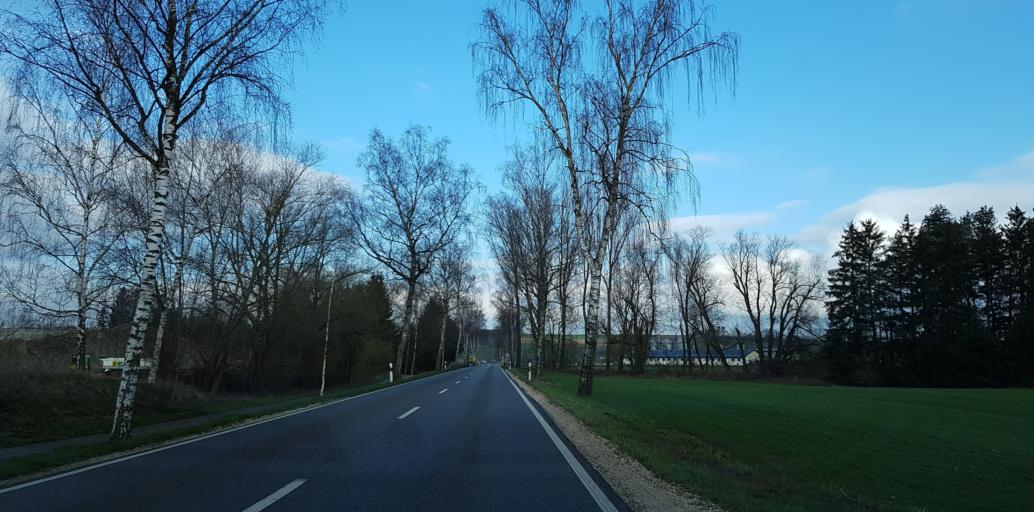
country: DE
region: Baden-Wuerttemberg
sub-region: Tuebingen Region
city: Erbach
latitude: 48.3303
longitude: 9.9210
